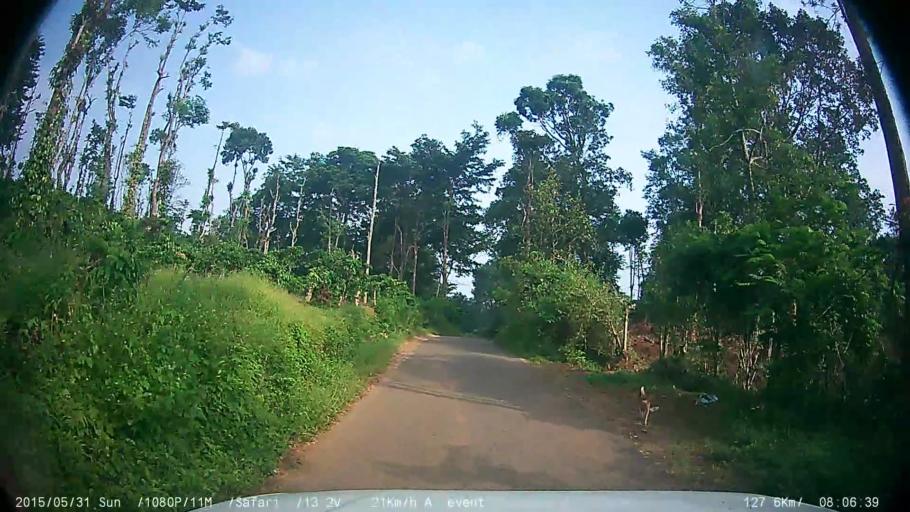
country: IN
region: Kerala
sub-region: Wayanad
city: Kalpetta
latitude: 11.6388
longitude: 76.0319
